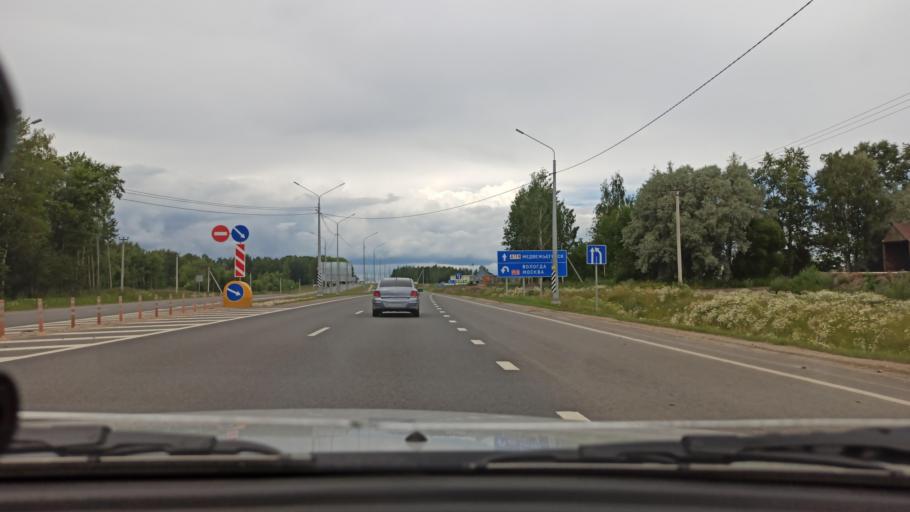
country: RU
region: Vologda
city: Molochnoye
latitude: 59.2551
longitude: 39.7602
